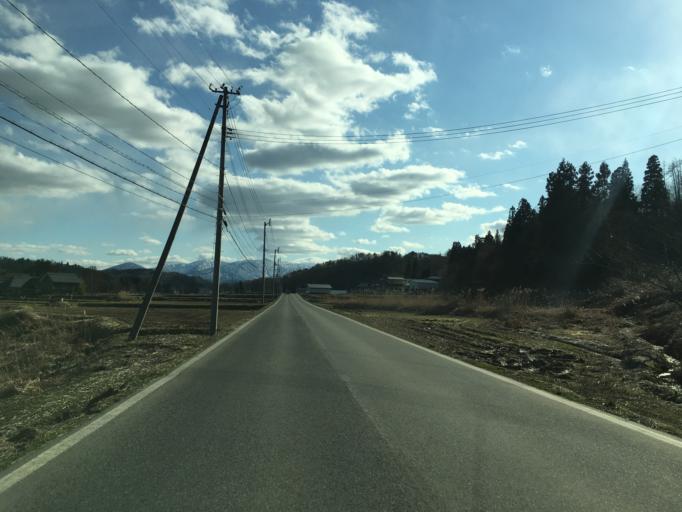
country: JP
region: Yamagata
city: Nagai
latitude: 37.9932
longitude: 140.0061
